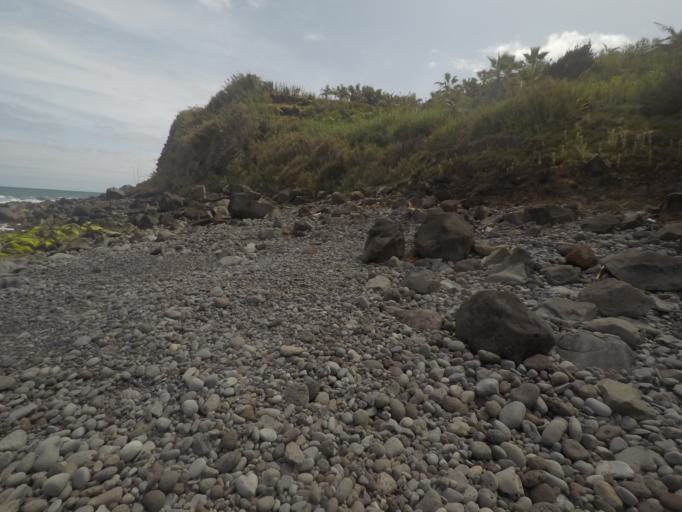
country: PT
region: Madeira
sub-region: Sao Vicente
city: Sao Vicente
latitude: 32.8245
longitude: -16.9969
